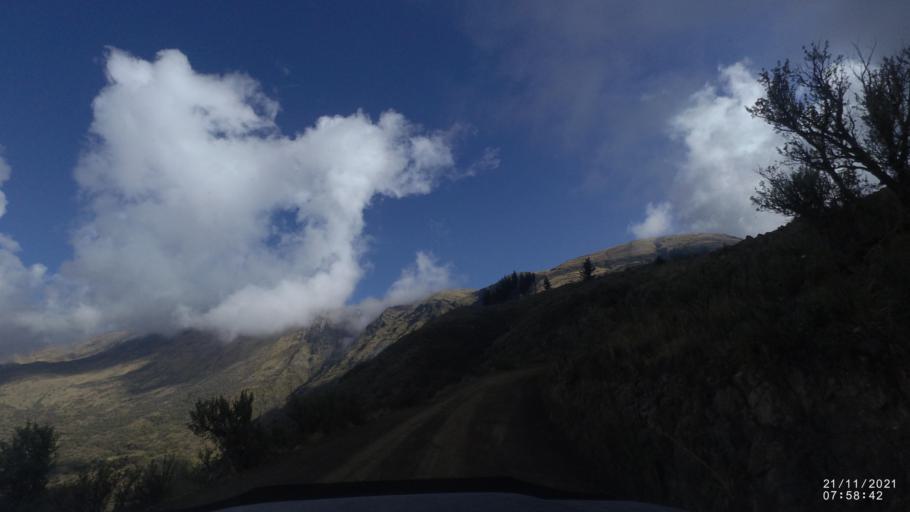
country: BO
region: Cochabamba
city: Cochabamba
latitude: -17.2935
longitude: -66.2203
